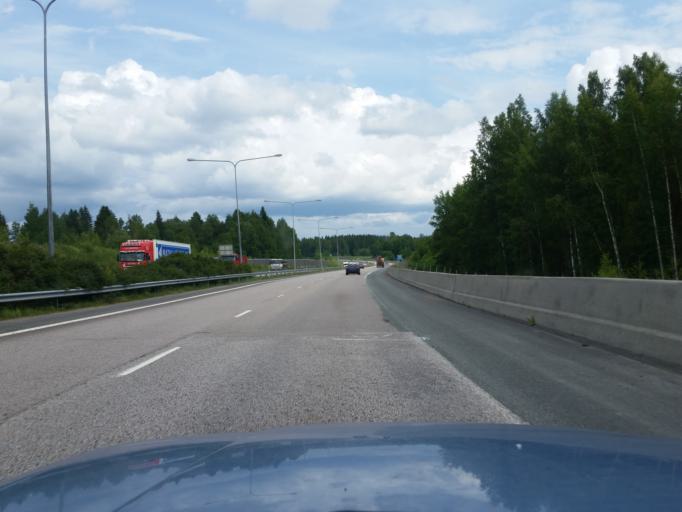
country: FI
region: Paijanne Tavastia
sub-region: Lahti
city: Lahti
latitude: 60.9915
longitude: 25.7546
